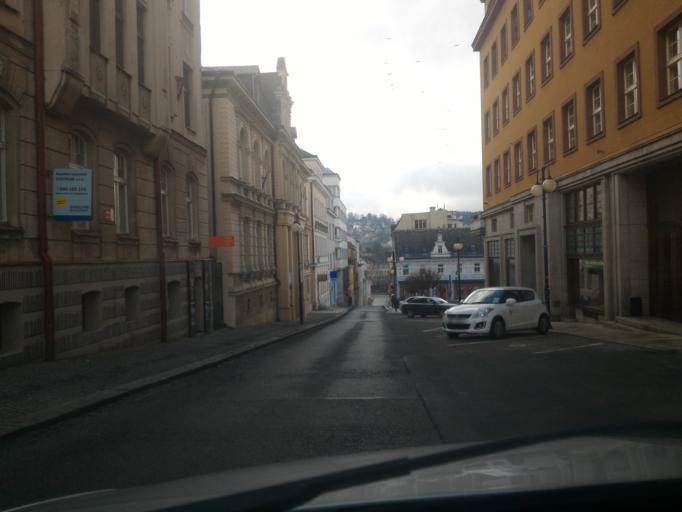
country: CZ
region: Liberecky
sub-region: Okres Jablonec nad Nisou
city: Jablonec nad Nisou
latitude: 50.7247
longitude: 15.1717
